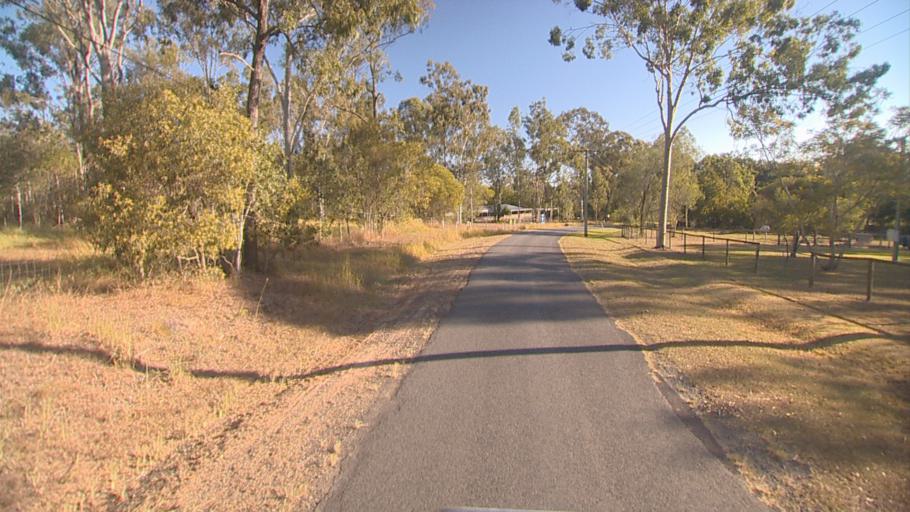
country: AU
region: Queensland
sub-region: Logan
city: North Maclean
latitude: -27.8127
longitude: 153.0462
